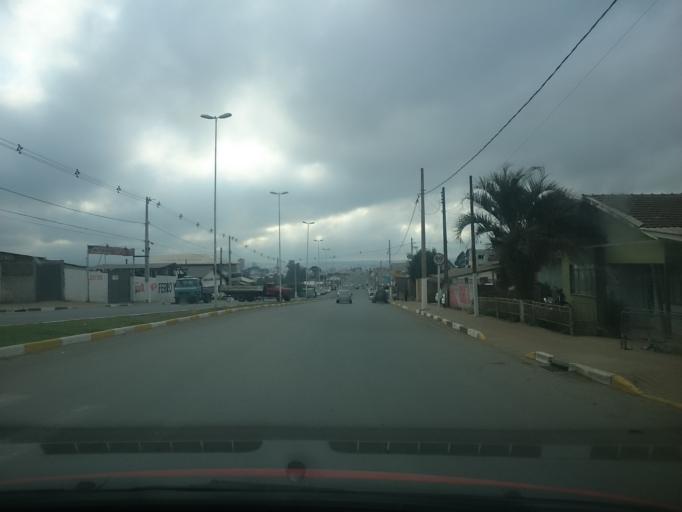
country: BR
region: Santa Catarina
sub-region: Lages
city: Lages
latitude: -27.8326
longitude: -50.3475
